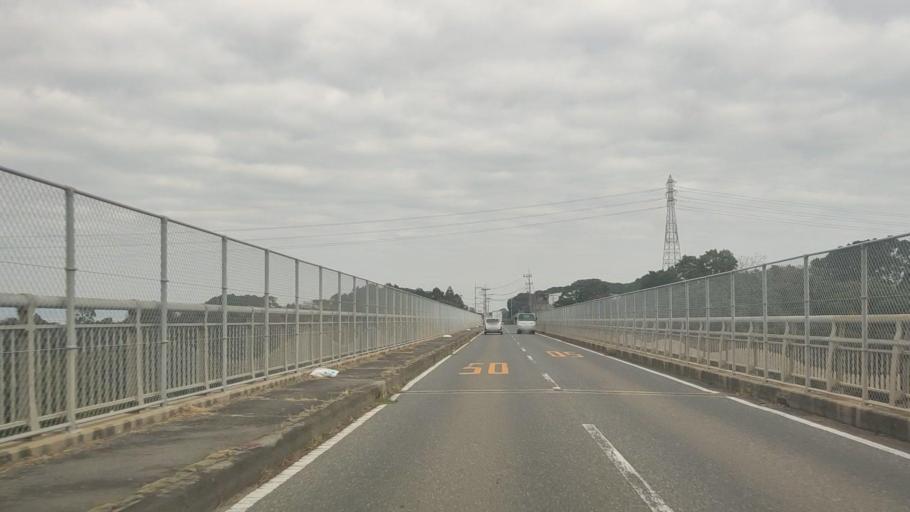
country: JP
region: Nagasaki
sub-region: Isahaya-shi
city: Isahaya
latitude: 32.8068
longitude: 130.1689
